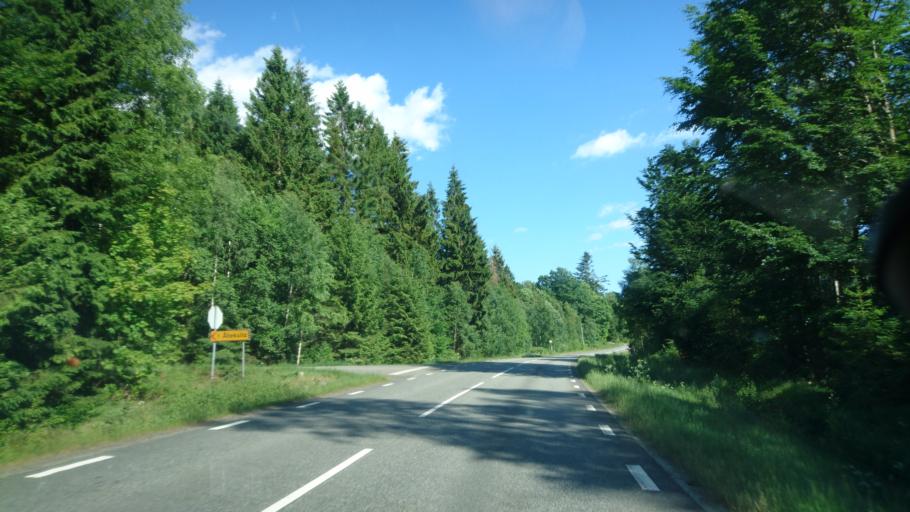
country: SE
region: Kronoberg
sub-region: Almhults Kommun
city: AElmhult
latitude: 56.4800
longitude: 14.2065
